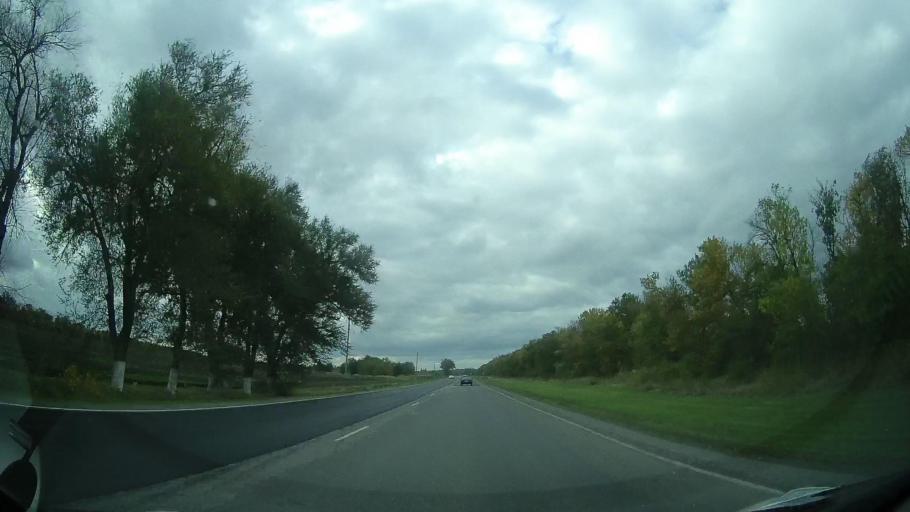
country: RU
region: Rostov
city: Zernograd
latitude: 46.7992
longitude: 40.3659
